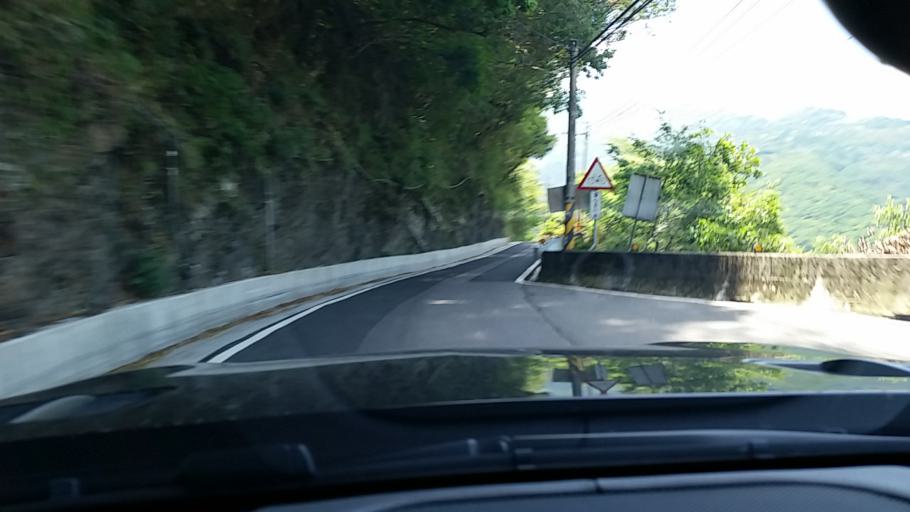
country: TW
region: Taiwan
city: Daxi
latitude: 24.6989
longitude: 121.3737
